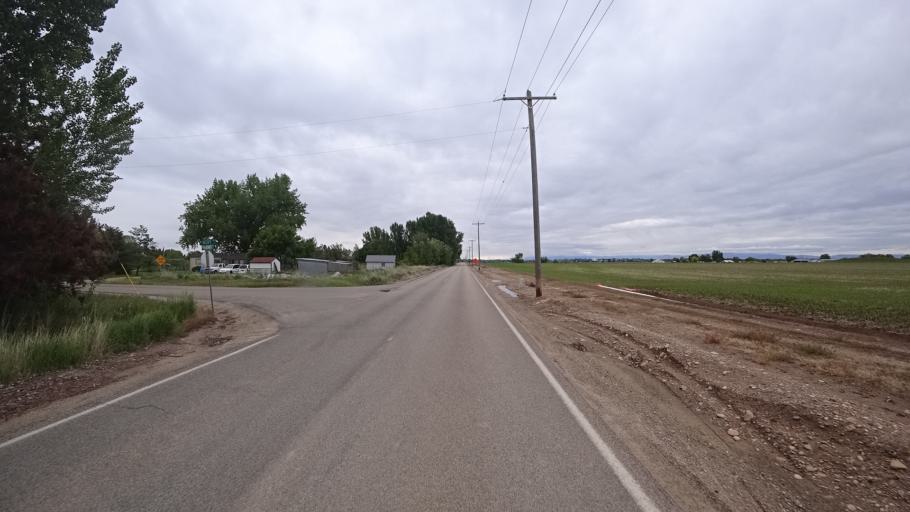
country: US
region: Idaho
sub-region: Ada County
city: Star
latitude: 43.6399
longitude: -116.4736
